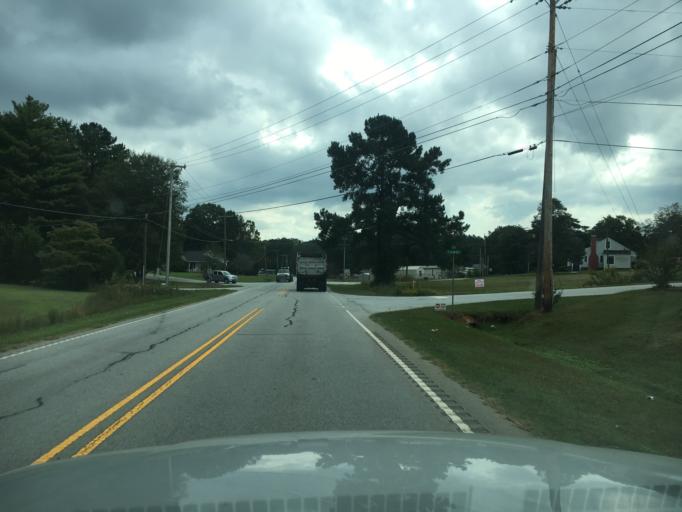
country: US
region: South Carolina
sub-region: Greenville County
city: Greer
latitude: 34.9718
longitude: -82.2387
